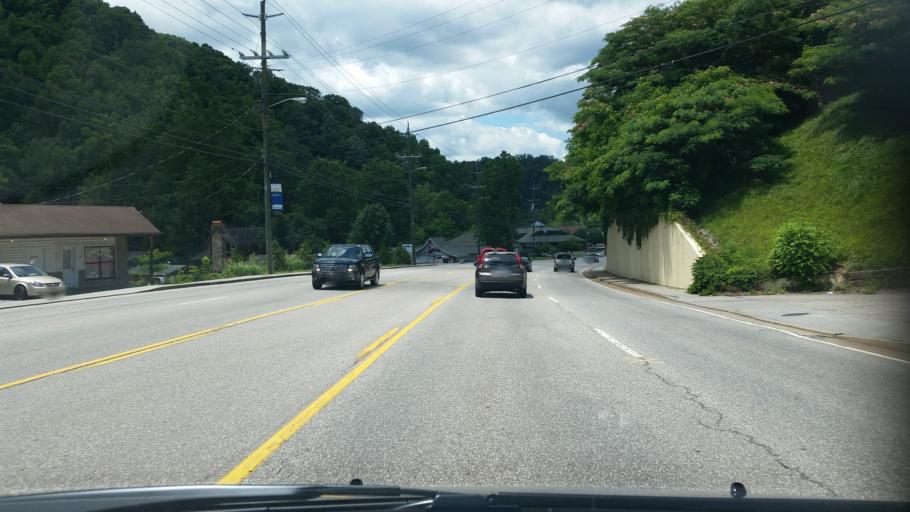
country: US
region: Tennessee
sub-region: Sevier County
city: Gatlinburg
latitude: 35.7246
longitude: -83.4920
